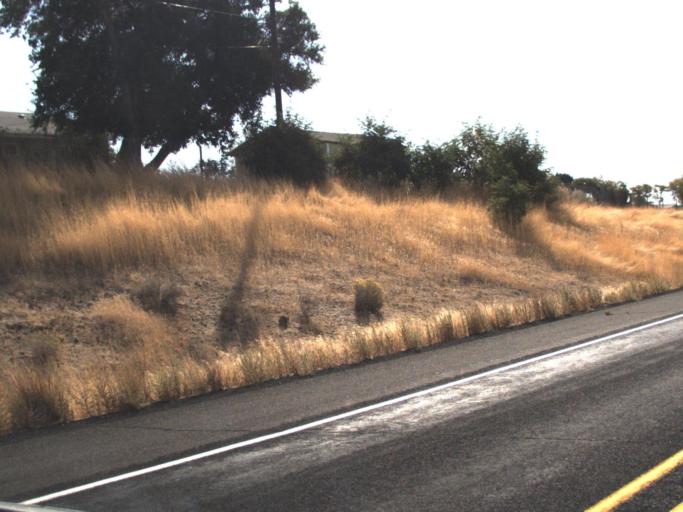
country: US
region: Washington
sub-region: Franklin County
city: Basin City
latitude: 46.5784
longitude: -119.0041
